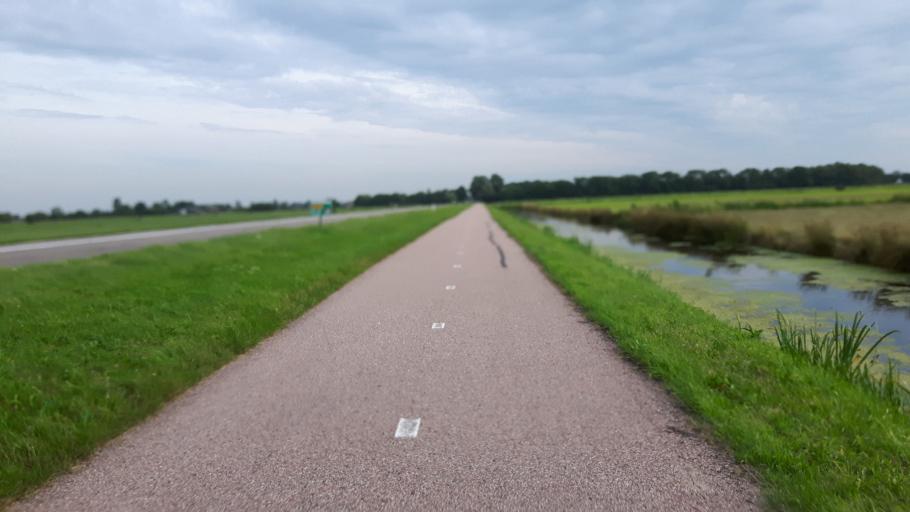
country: NL
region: Utrecht
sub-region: Gemeente Woerden
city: Woerden
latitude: 52.1382
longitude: 4.9118
